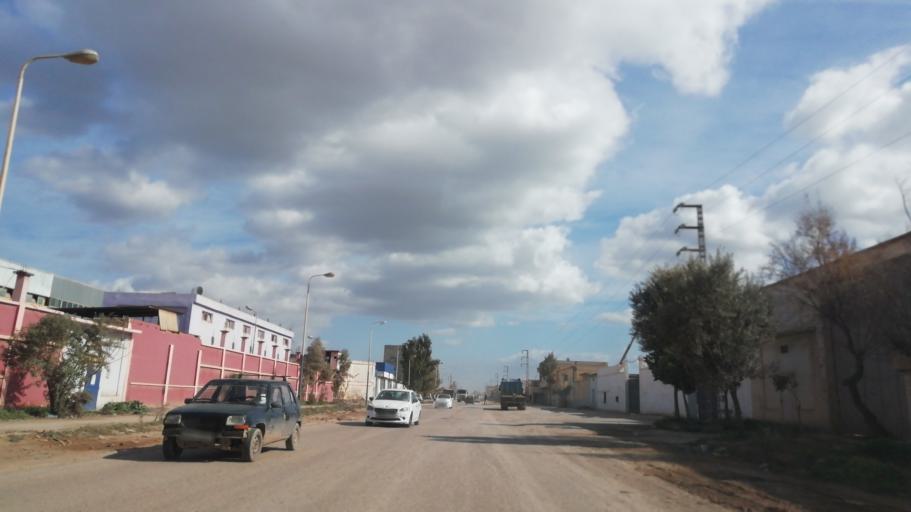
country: DZ
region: Oran
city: Es Senia
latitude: 35.6512
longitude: -0.5864
